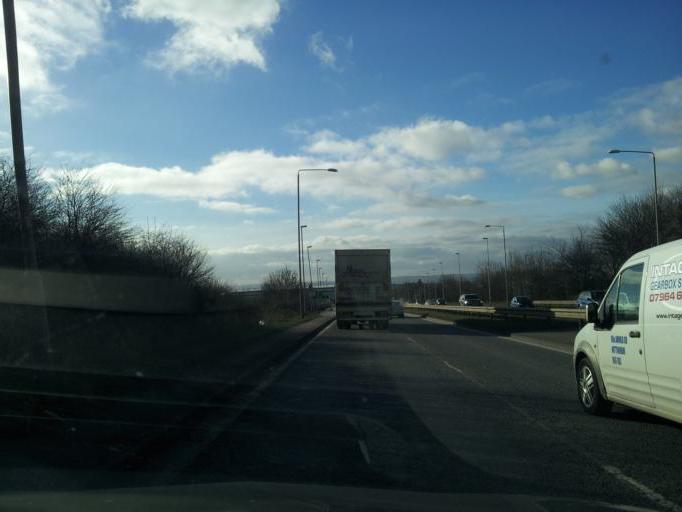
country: GB
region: England
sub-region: Derbyshire
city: Pinxton
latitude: 53.1119
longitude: -1.2919
